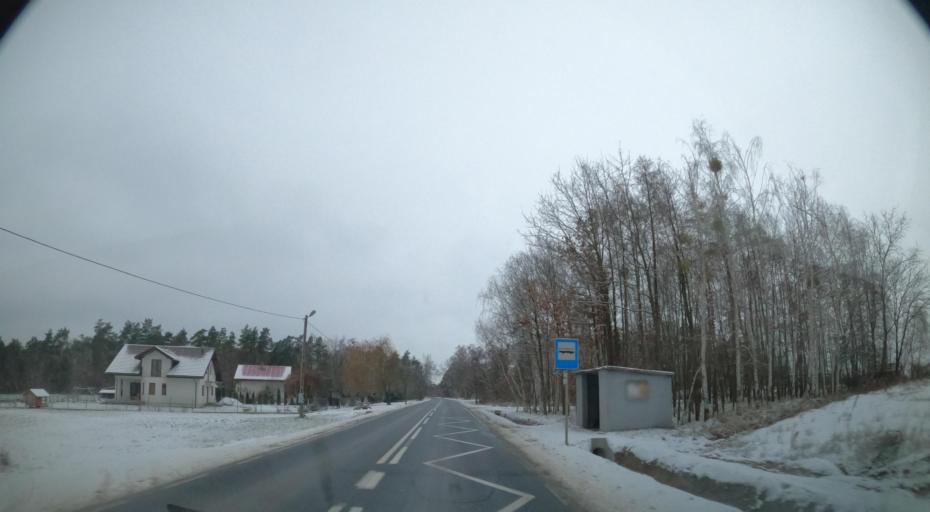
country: PL
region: Masovian Voivodeship
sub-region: Powiat plocki
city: Nowy Duninow
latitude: 52.6107
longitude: 19.4716
